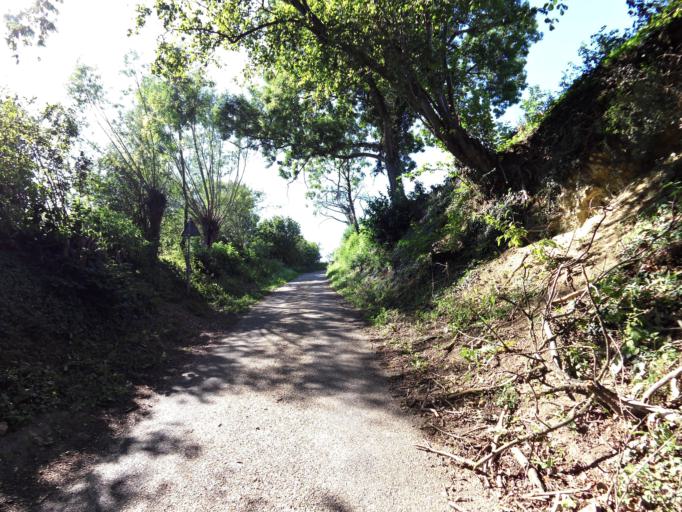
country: NL
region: Limburg
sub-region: Gemeente Voerendaal
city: Ubachsberg
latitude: 50.8215
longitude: 5.9454
